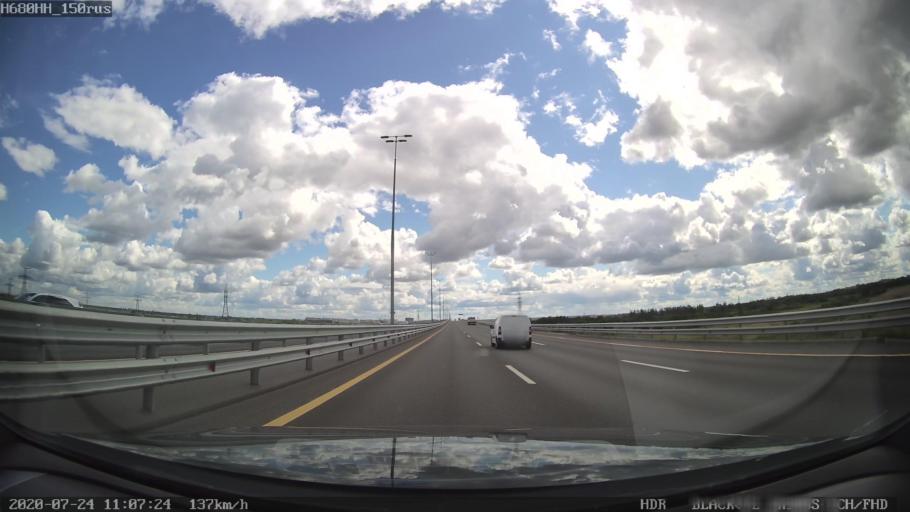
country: RU
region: St.-Petersburg
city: Pushkin
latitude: 59.7561
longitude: 30.4038
